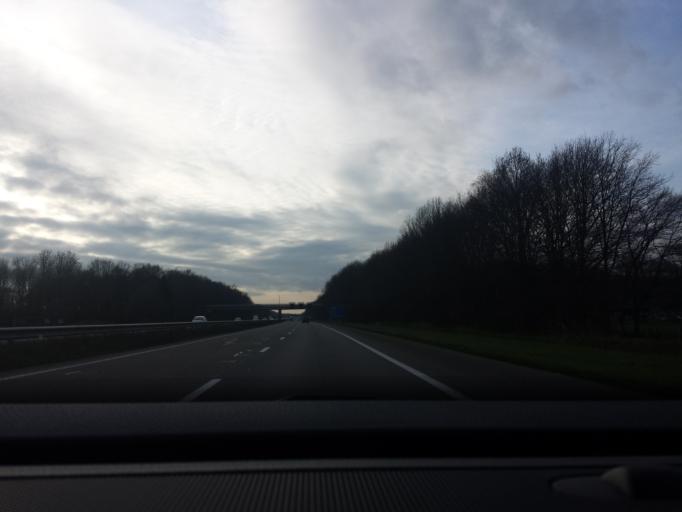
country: NL
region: Gelderland
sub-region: Gemeente Doesburg
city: Doesburg
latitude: 51.9339
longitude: 6.1706
